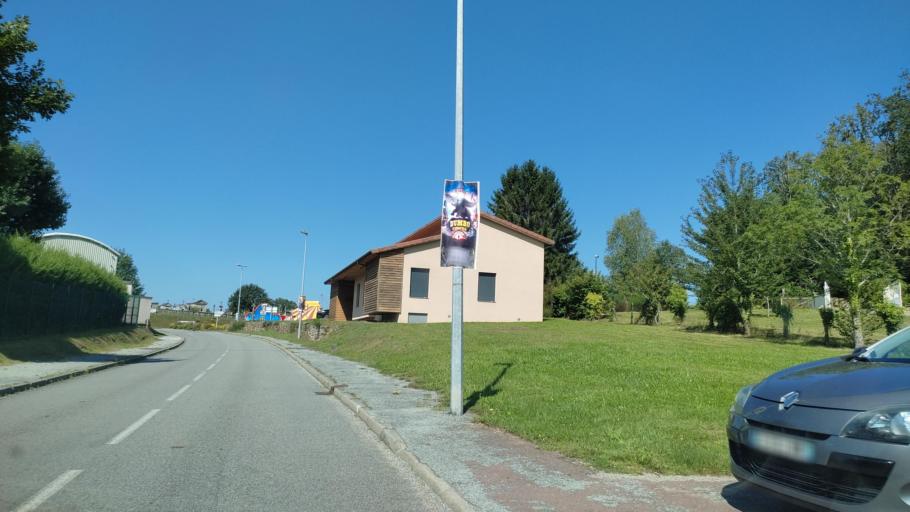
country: FR
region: Limousin
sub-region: Departement de la Haute-Vienne
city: Razes
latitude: 46.0325
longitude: 1.3429
